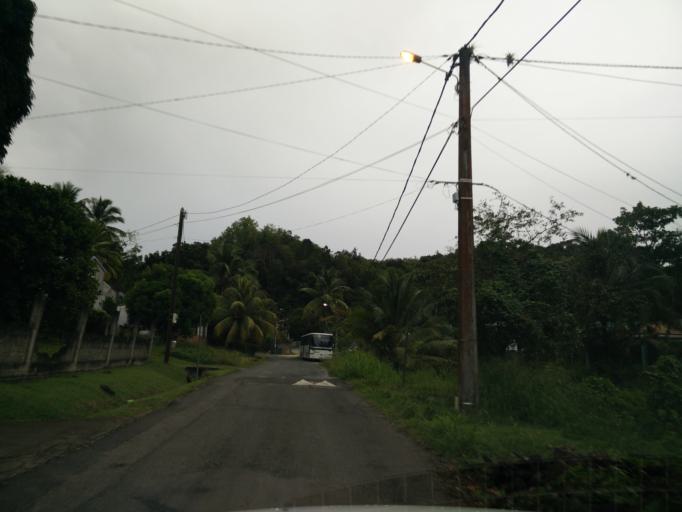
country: GP
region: Guadeloupe
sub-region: Guadeloupe
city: Le Gosier
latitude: 16.2262
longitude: -61.4997
